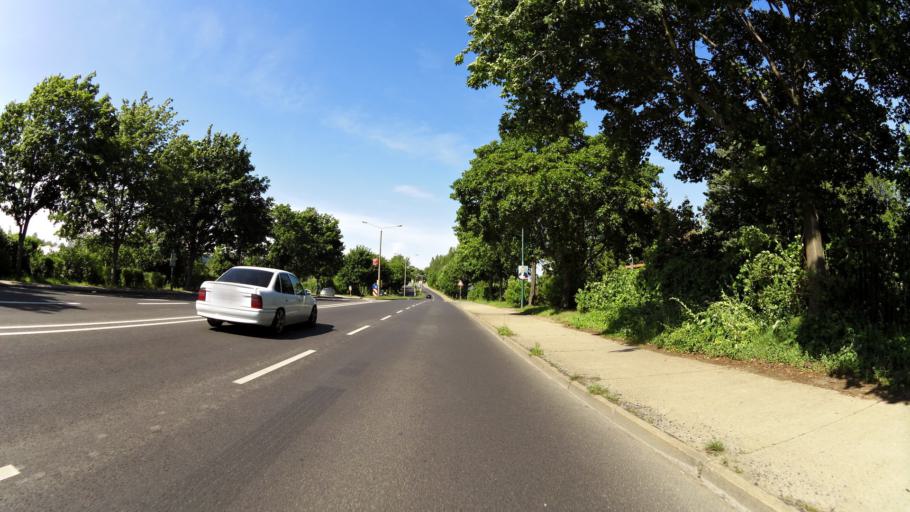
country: DE
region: Brandenburg
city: Frankfurt (Oder)
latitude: 52.3577
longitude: 14.5317
